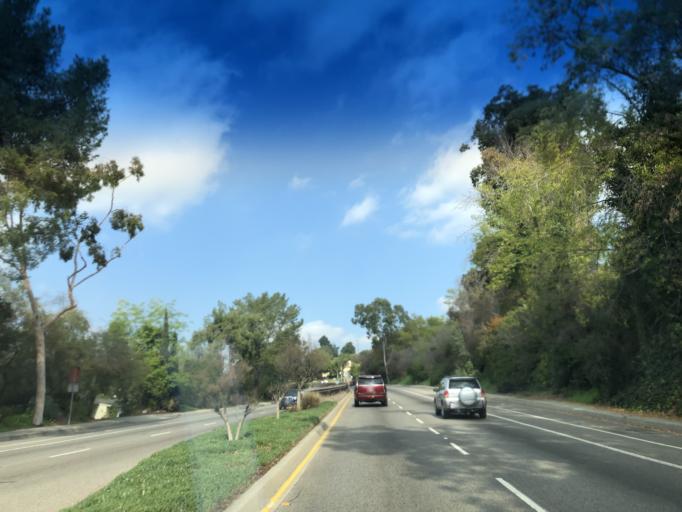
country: US
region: California
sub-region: Los Angeles County
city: East La Mirada
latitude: 33.9553
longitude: -118.0022
